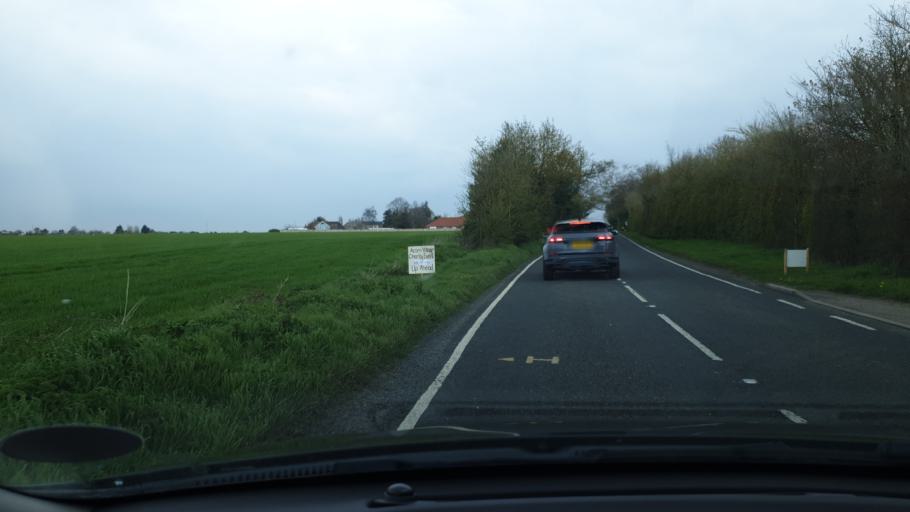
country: GB
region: England
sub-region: Essex
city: Manningtree
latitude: 51.9366
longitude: 1.0625
